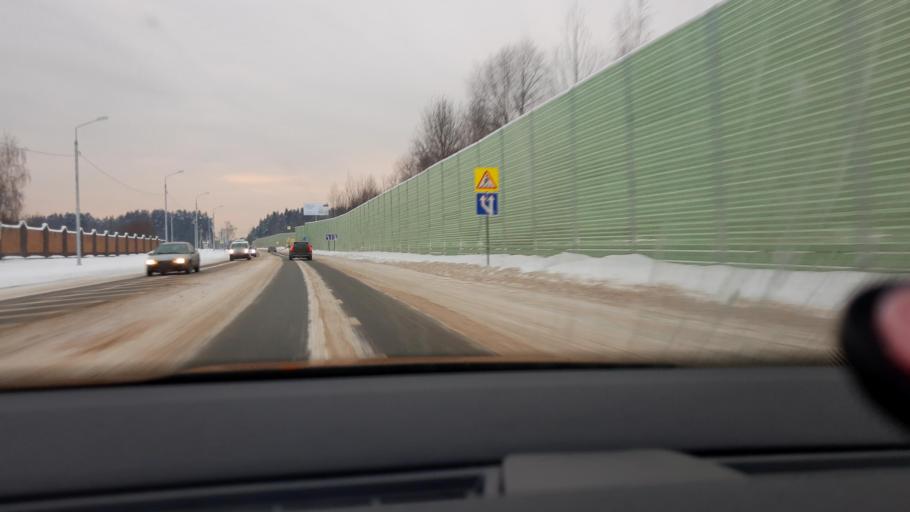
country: RU
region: Moskovskaya
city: Rozhdestveno
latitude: 55.8080
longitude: 36.9656
